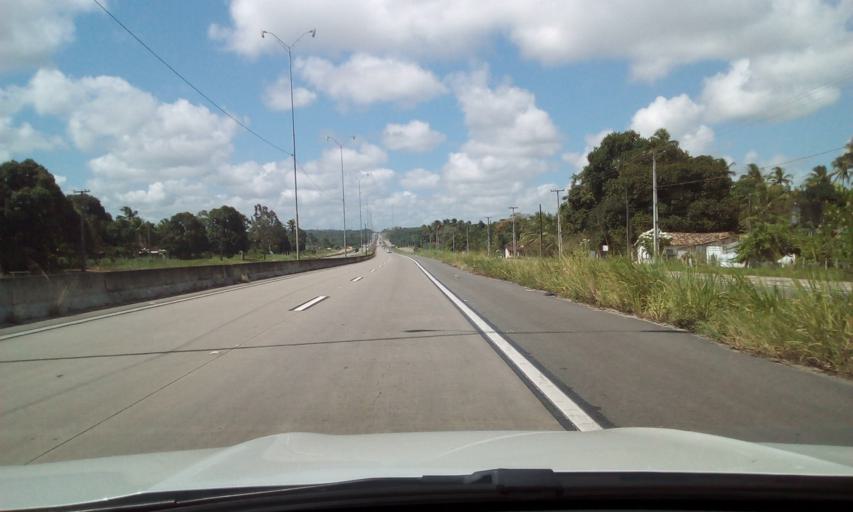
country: BR
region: Paraiba
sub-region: Conde
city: Conde
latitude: -7.3437
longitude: -34.9479
